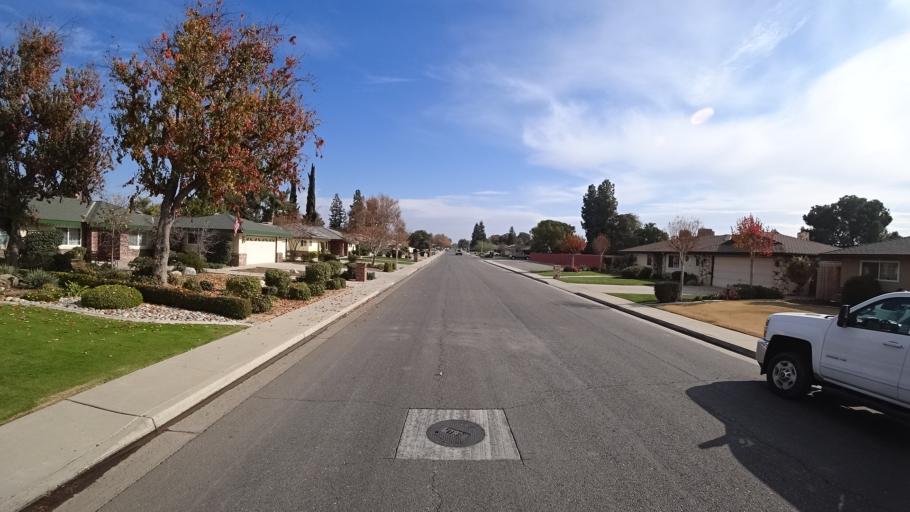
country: US
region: California
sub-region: Kern County
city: Greenacres
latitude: 35.4095
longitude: -119.0888
